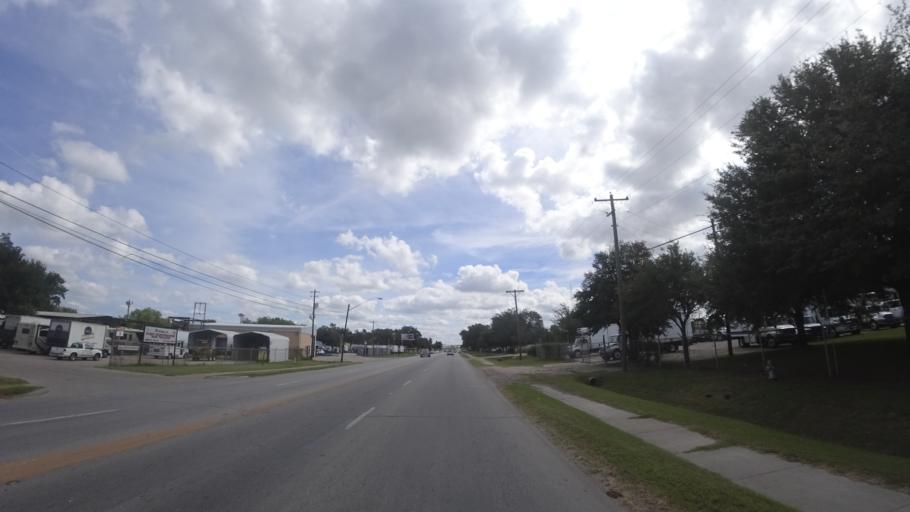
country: US
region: Texas
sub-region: Travis County
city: Austin
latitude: 30.2549
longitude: -97.7000
